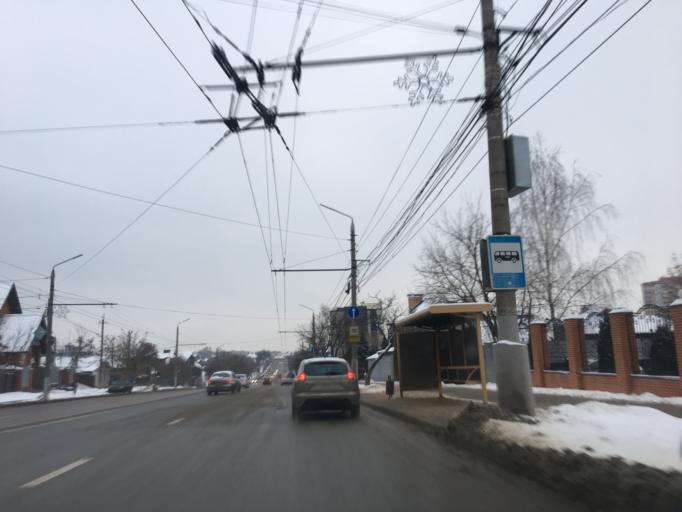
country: RU
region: Tula
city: Tula
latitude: 54.1891
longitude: 37.5826
